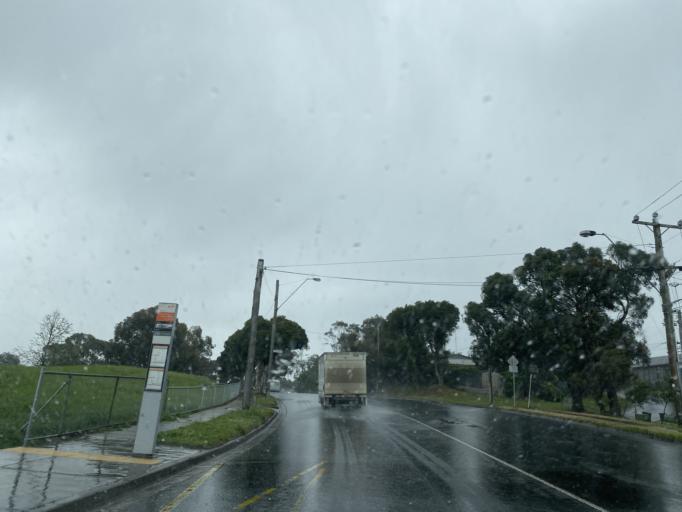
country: AU
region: Victoria
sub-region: Banyule
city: Montmorency
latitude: -37.7134
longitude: 145.1149
